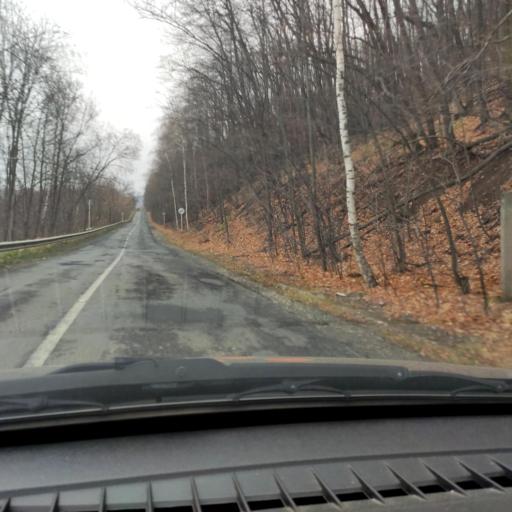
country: RU
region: Samara
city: Povolzhskiy
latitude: 53.4386
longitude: 49.6932
